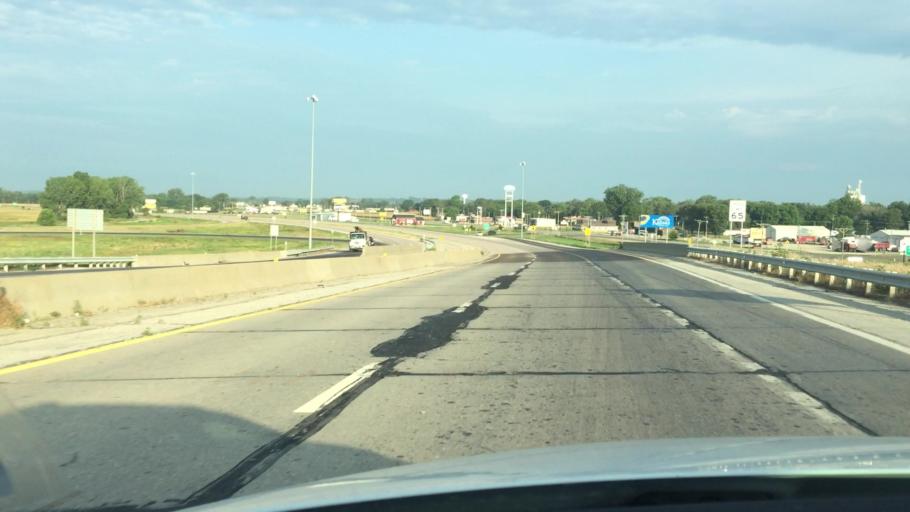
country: US
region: Kansas
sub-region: Doniphan County
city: Elwood
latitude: 39.7497
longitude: -94.8649
